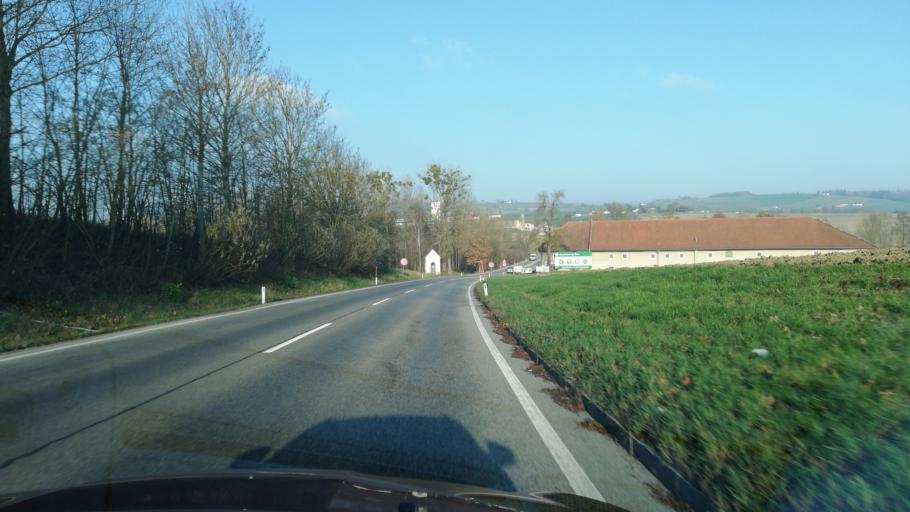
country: AT
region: Upper Austria
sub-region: Wels-Land
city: Buchkirchen
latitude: 48.2203
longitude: 14.0310
